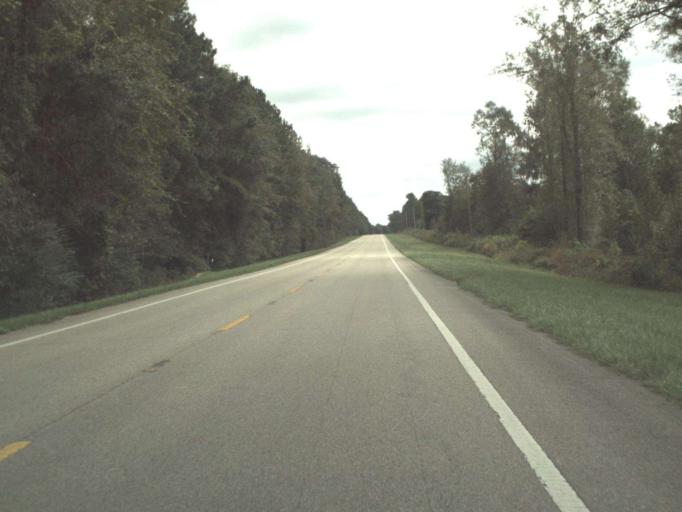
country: US
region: Florida
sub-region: Jackson County
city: Marianna
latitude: 30.6666
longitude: -85.2309
